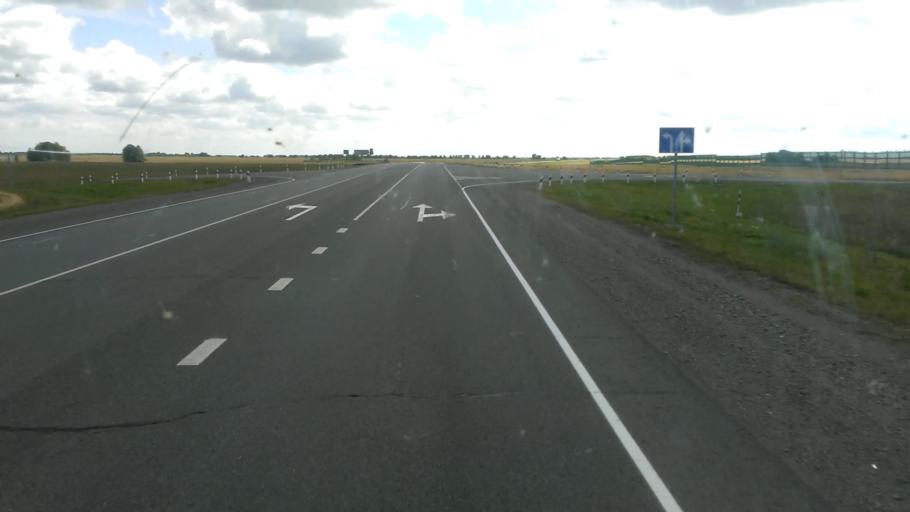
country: RU
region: Altai Krai
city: Troitskoye
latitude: 52.9171
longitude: 84.8120
